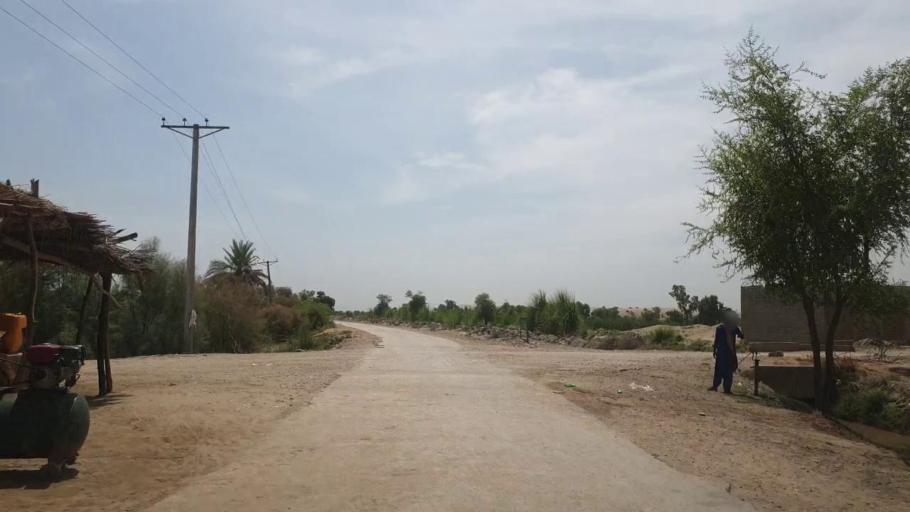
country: PK
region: Sindh
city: Kot Diji
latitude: 27.1103
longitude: 69.0219
